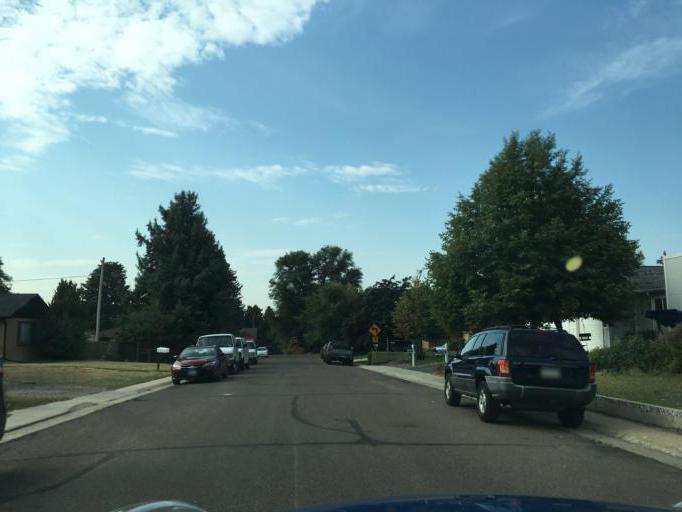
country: US
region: Colorado
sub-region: Jefferson County
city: Wheat Ridge
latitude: 39.7459
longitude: -105.1080
